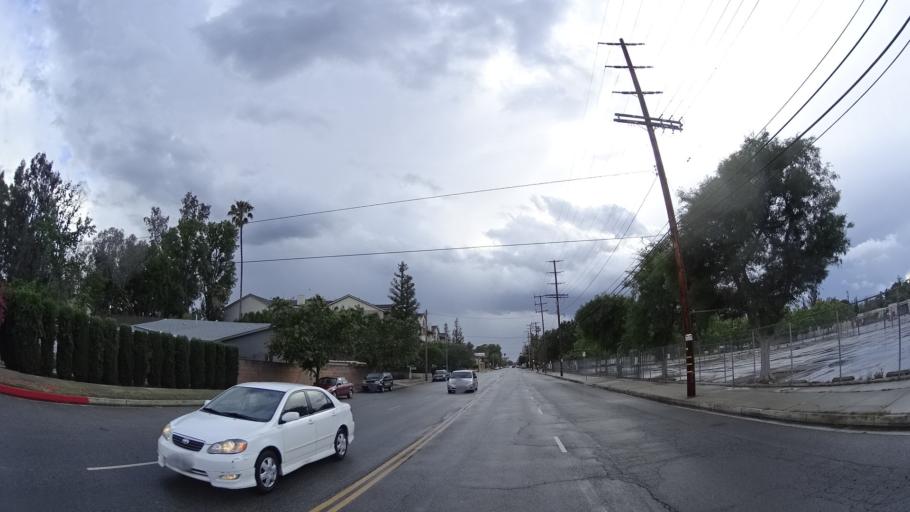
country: US
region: California
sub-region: Los Angeles County
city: Sherman Oaks
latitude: 34.1649
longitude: -118.4383
